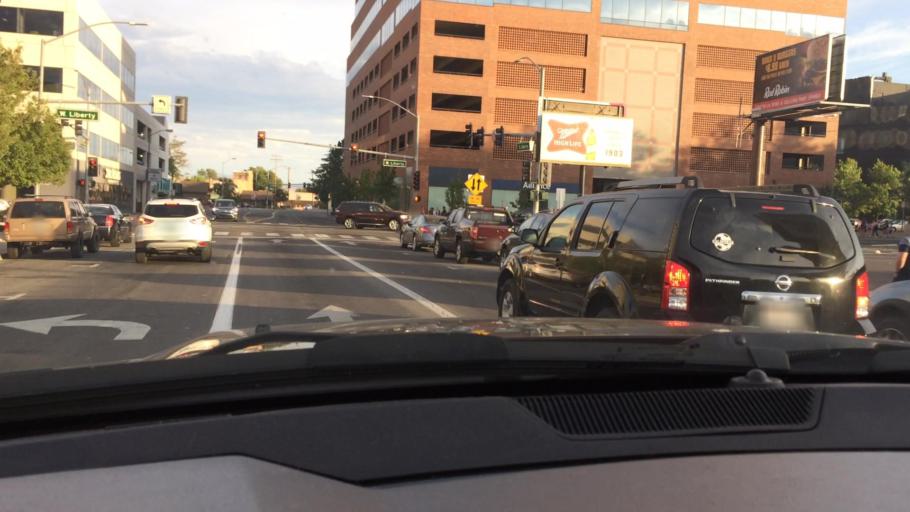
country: US
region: Nevada
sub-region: Washoe County
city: Reno
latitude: 39.5221
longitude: -119.8127
